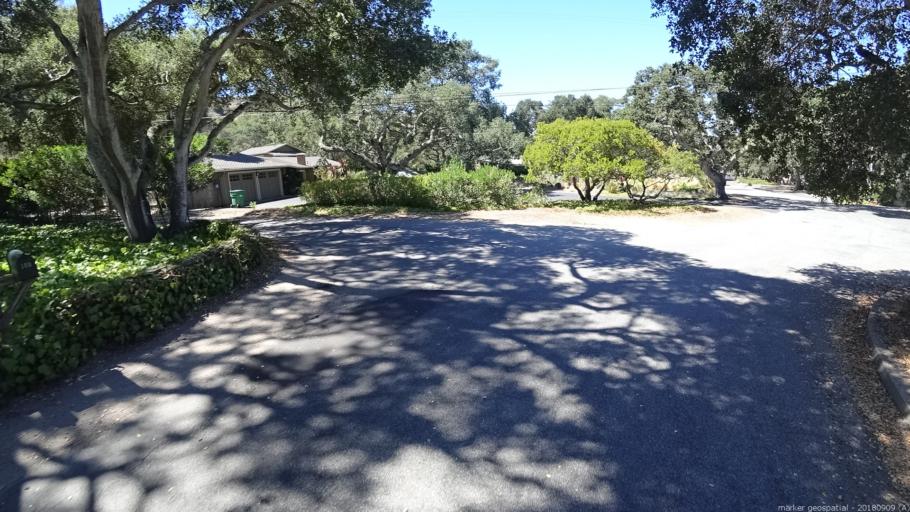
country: US
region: California
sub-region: Monterey County
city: Carmel Valley Village
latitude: 36.5713
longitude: -121.7139
